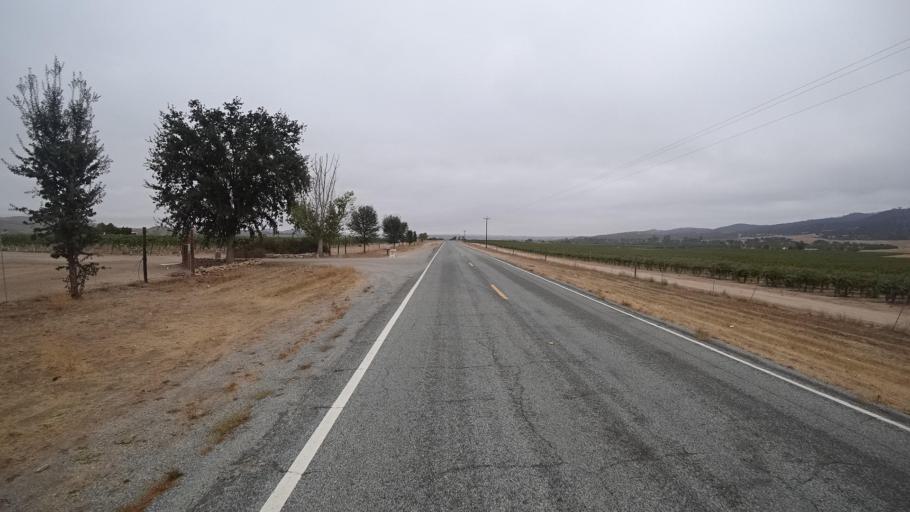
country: US
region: California
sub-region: San Luis Obispo County
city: Lake Nacimiento
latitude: 35.8810
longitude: -120.9058
